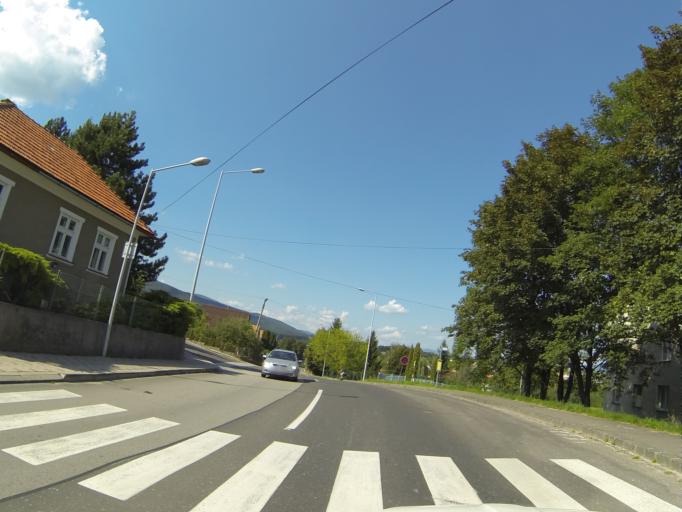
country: SK
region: Nitriansky
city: Bojnice
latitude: 48.7873
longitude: 18.5867
